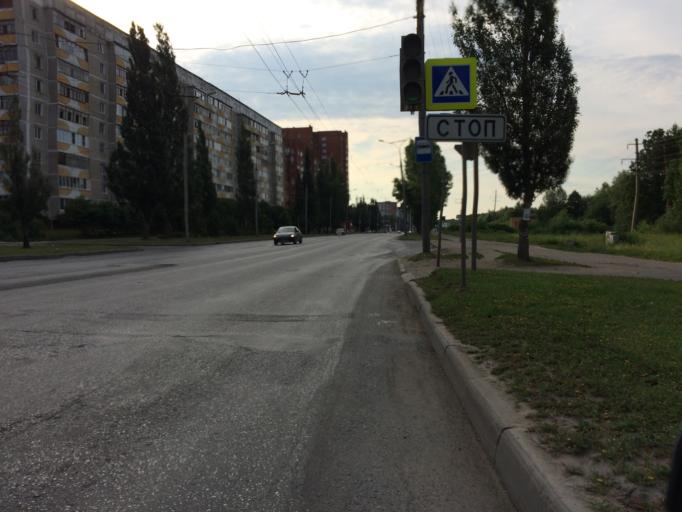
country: RU
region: Mariy-El
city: Yoshkar-Ola
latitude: 56.6262
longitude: 47.9197
